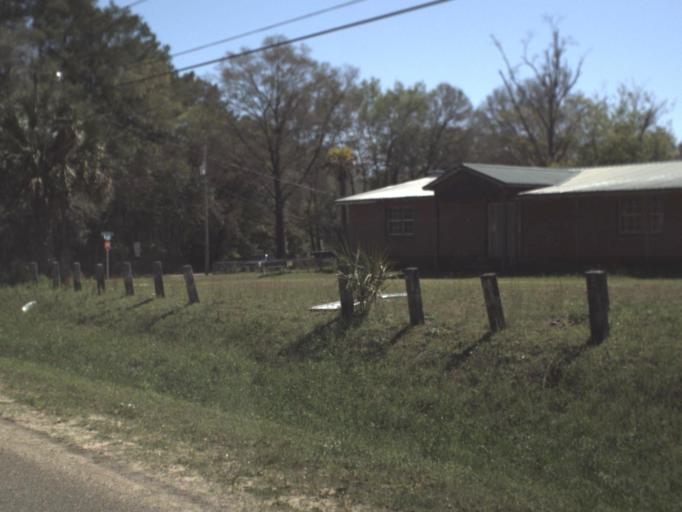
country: US
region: Florida
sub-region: Leon County
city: Tallahassee
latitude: 30.3784
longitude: -84.3009
